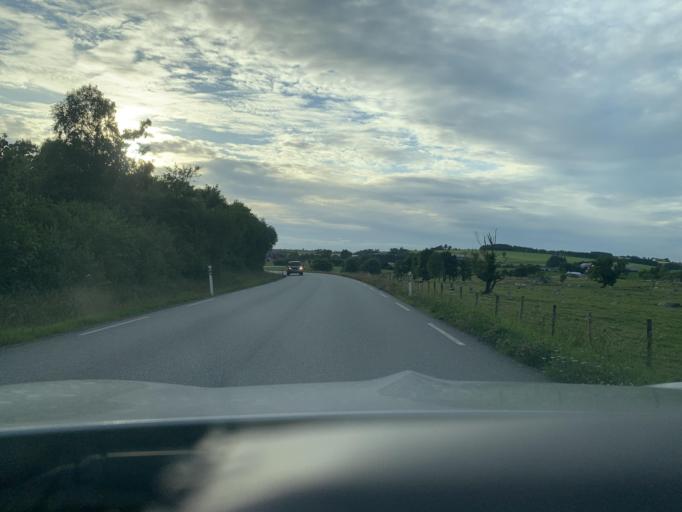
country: NO
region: Rogaland
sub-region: Time
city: Bryne
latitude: 58.6993
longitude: 5.7087
